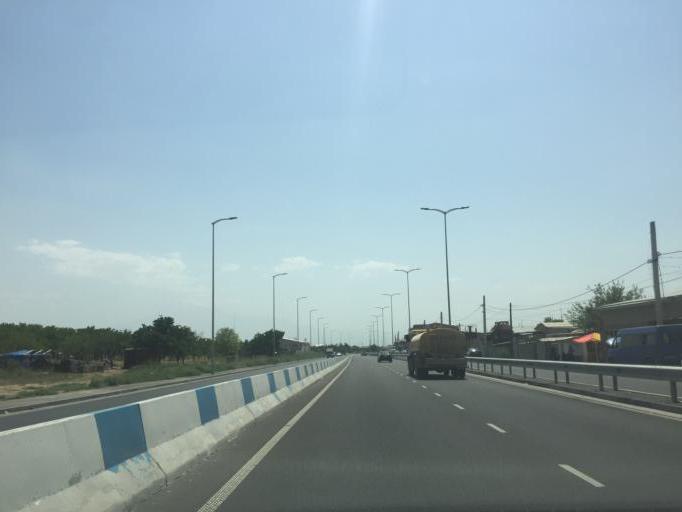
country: AM
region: Ararat
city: Norabats'
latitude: 40.1135
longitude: 44.4763
